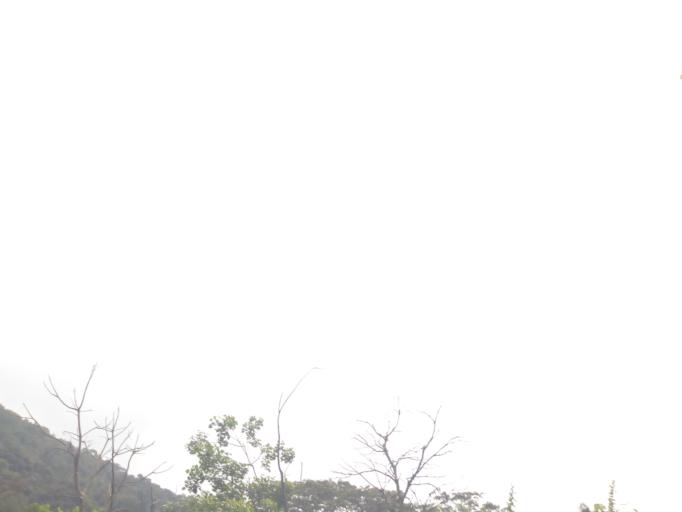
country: IN
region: Karnataka
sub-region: Dakshina Kannada
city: Sulya
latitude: 12.3813
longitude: 75.5115
